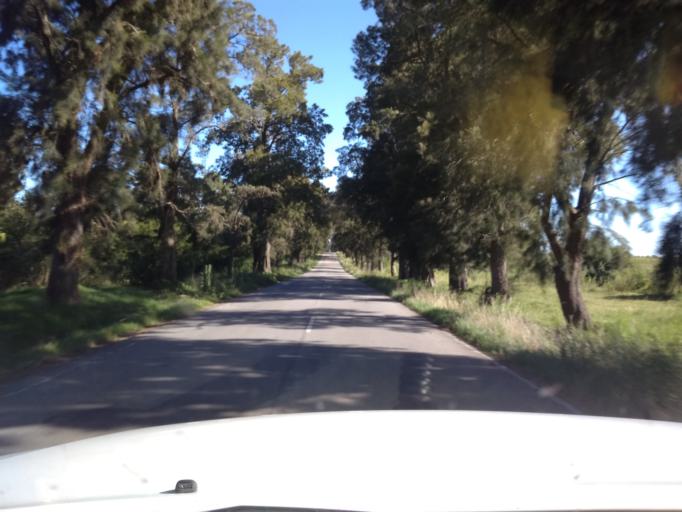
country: UY
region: Canelones
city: San Bautista
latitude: -34.3738
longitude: -55.9595
